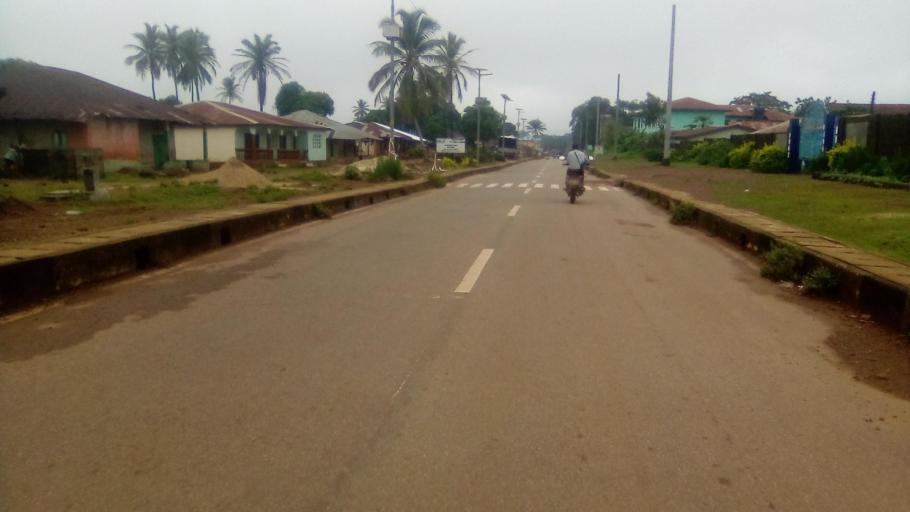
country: SL
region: Southern Province
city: Moyamba
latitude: 8.1524
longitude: -12.4318
